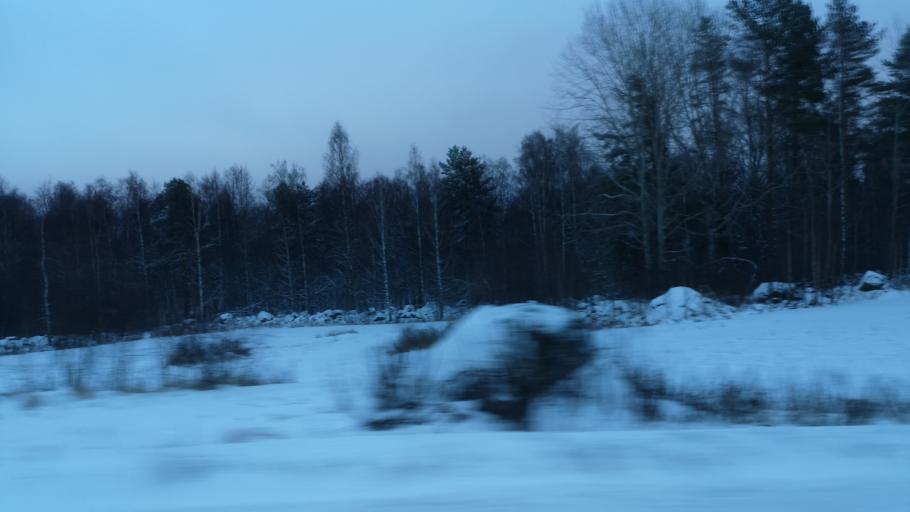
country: FI
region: Southern Savonia
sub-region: Savonlinna
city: Enonkoski
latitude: 62.1031
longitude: 28.6468
